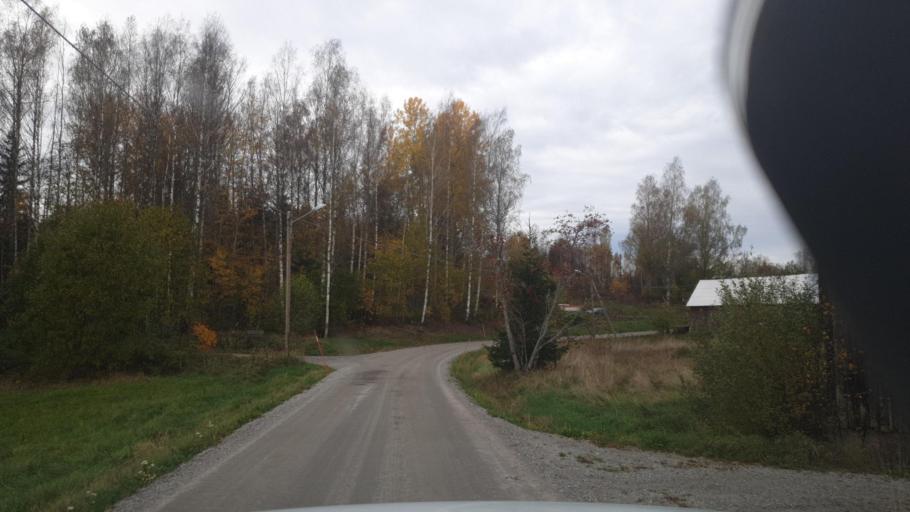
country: SE
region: Vaermland
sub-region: Arvika Kommun
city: Arvika
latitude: 59.6720
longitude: 12.7682
